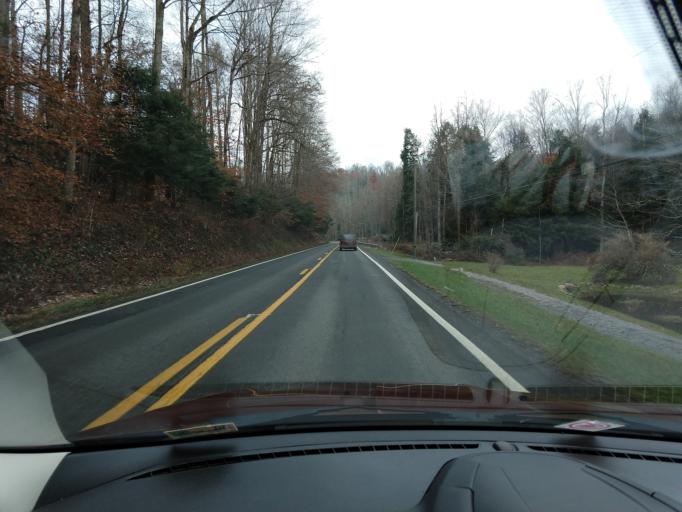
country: US
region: West Virginia
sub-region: Nicholas County
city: Craigsville
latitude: 38.2606
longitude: -80.7312
